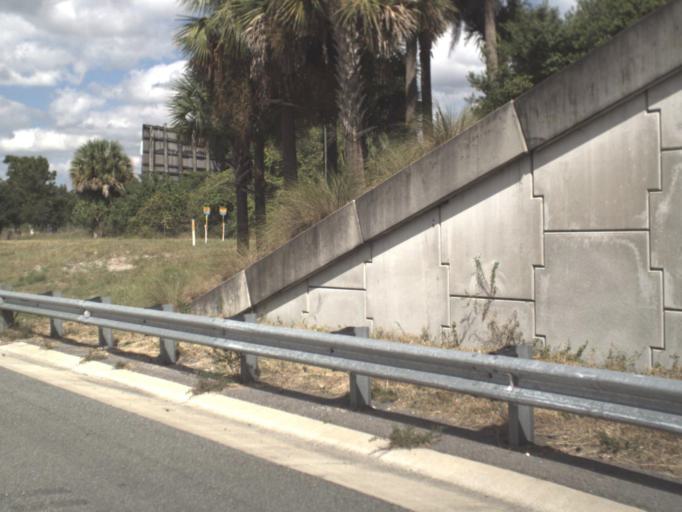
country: US
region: Florida
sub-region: Orange County
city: Orlovista
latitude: 28.5033
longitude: -81.4840
